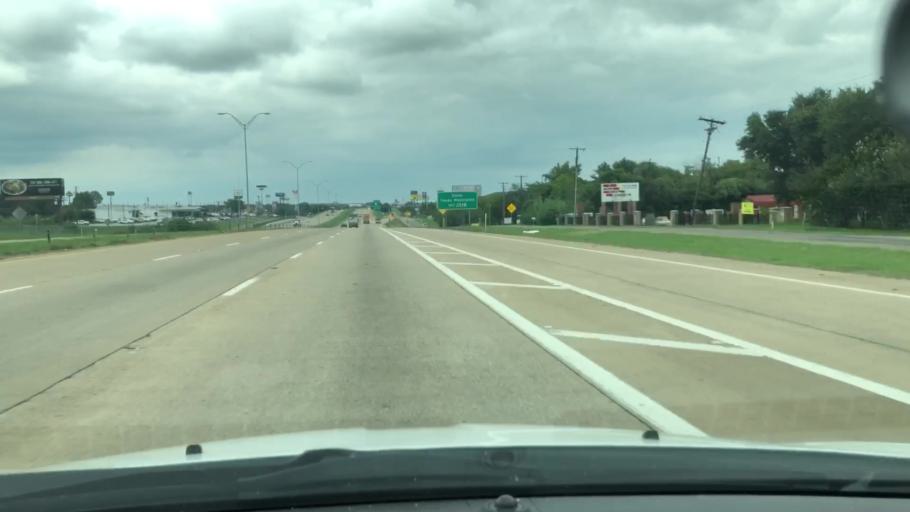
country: US
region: Texas
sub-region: Ellis County
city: Ennis
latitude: 32.3278
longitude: -96.6110
